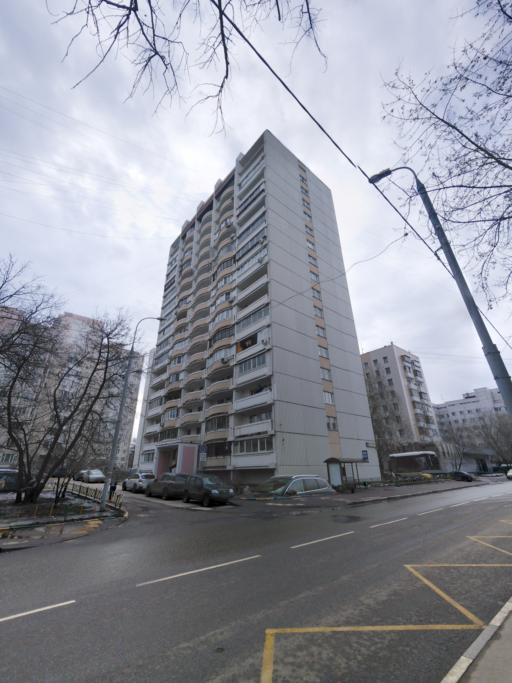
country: RU
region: Moscow
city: Mar'ina Roshcha
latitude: 55.8005
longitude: 37.5717
